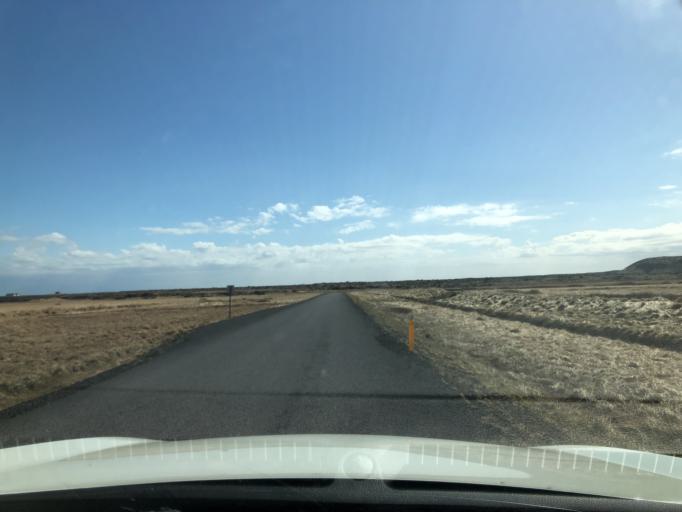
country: IS
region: West
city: Olafsvik
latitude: 64.8334
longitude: -23.4073
